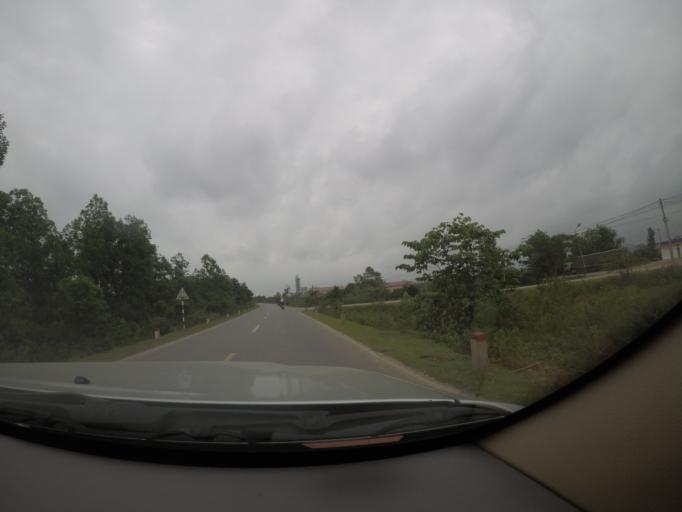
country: VN
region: Quang Binh
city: Kien Giang
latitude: 17.2660
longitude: 106.6627
